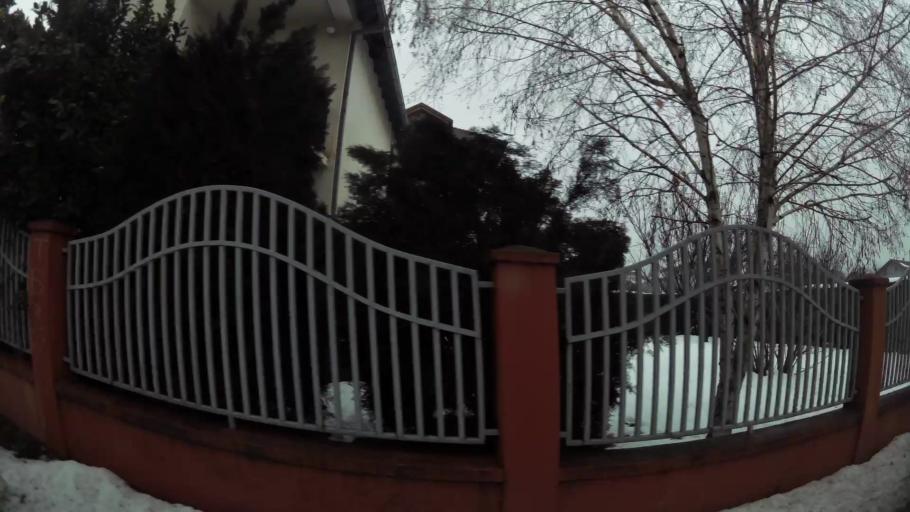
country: RS
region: Central Serbia
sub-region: Belgrade
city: Zemun
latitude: 44.8518
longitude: 20.3660
